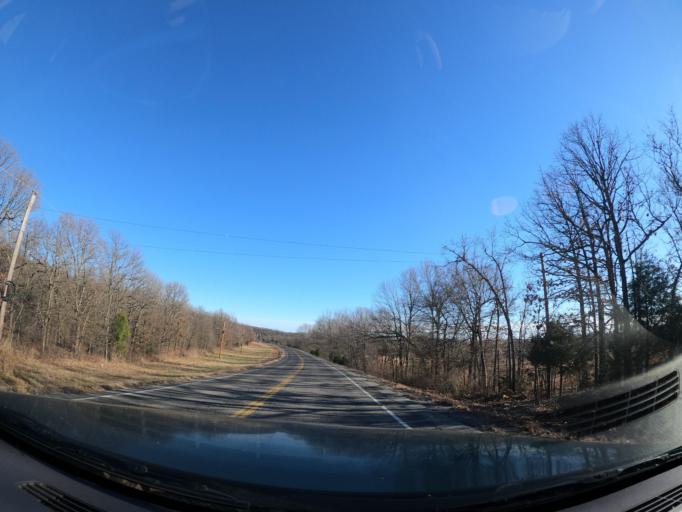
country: US
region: Oklahoma
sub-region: Pittsburg County
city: Longtown
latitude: 35.2162
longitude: -95.4232
